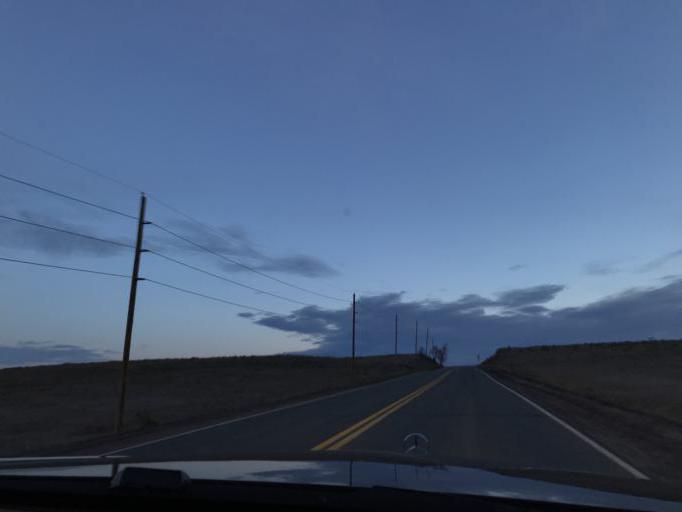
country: US
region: Colorado
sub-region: Boulder County
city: Superior
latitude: 39.8834
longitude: -105.1655
